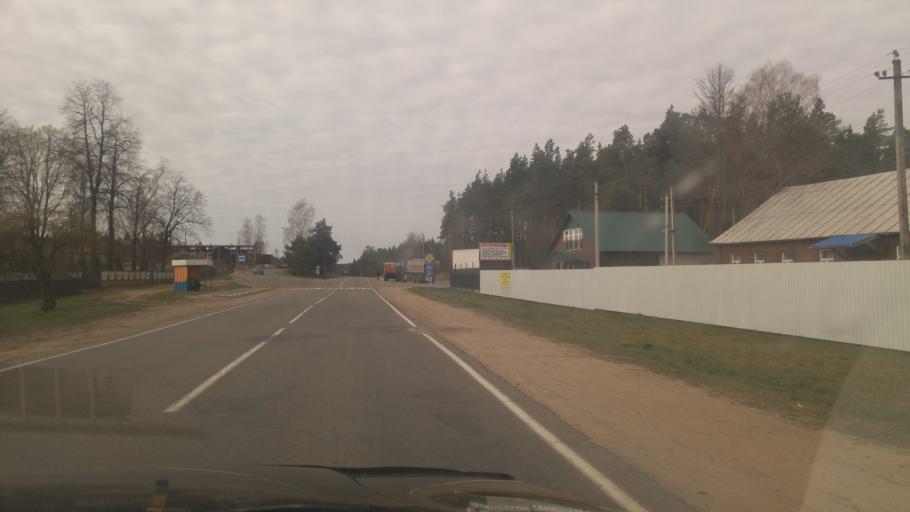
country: BY
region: Minsk
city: Chervyen'
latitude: 53.7009
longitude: 28.4069
